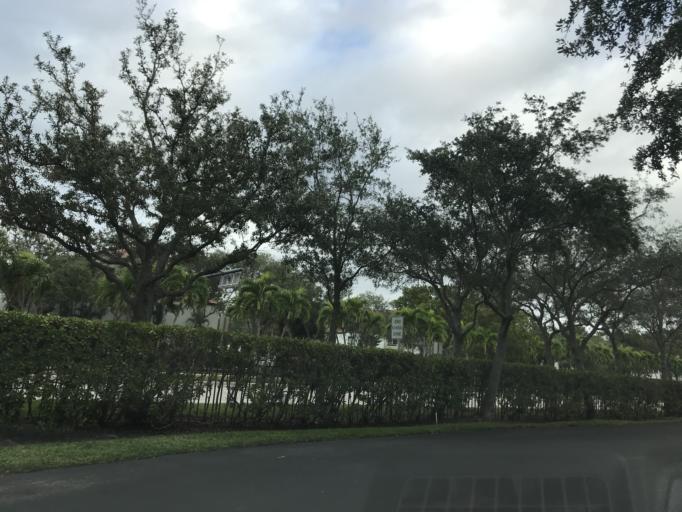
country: US
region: Florida
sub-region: Broward County
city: Coral Springs
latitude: 26.2982
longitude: -80.2822
